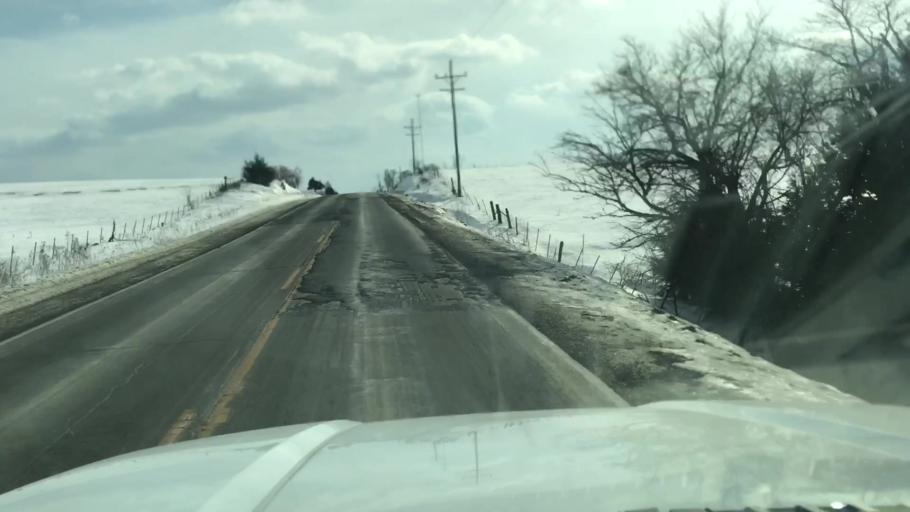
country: US
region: Missouri
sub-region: Gentry County
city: Stanberry
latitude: 40.3780
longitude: -94.6472
